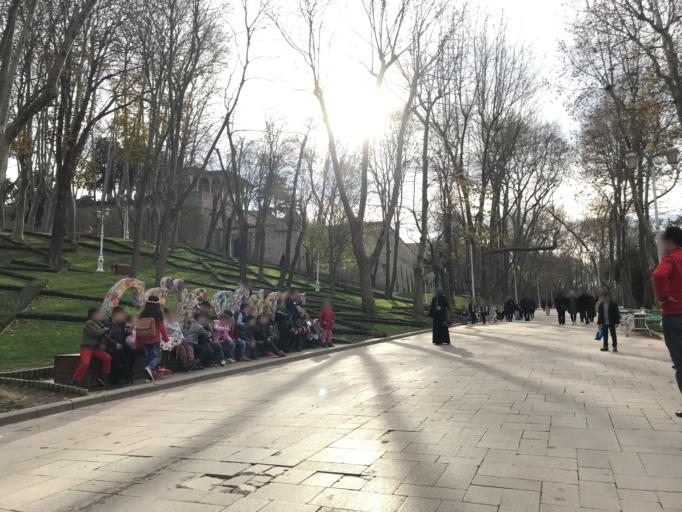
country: TR
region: Istanbul
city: Eminoenue
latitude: 41.0155
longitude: 28.9848
